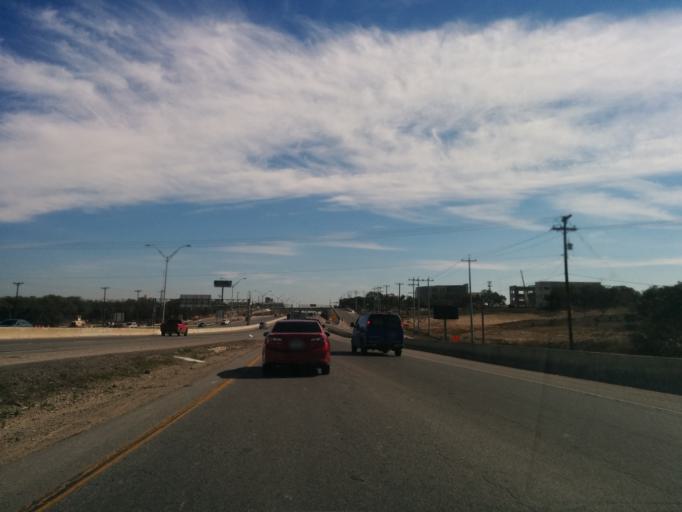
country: US
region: Texas
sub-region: Bexar County
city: Shavano Park
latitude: 29.5910
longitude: -98.5956
